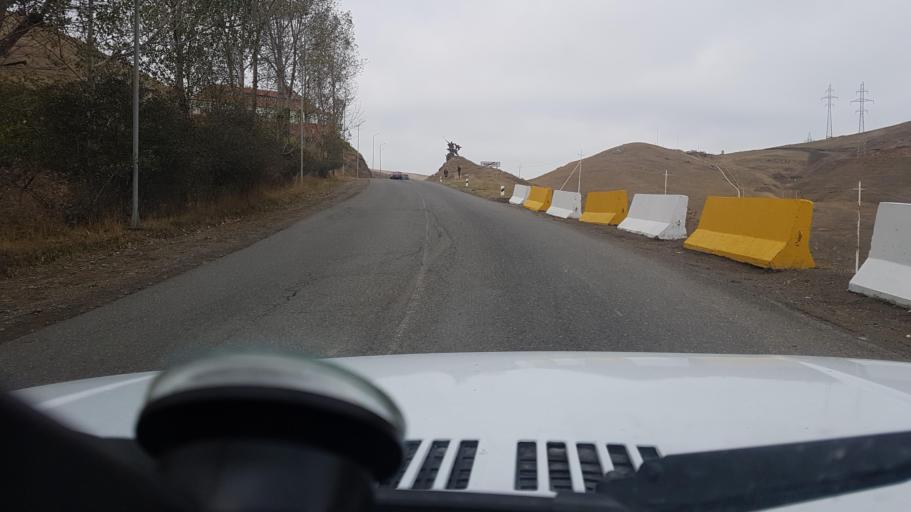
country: AZ
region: Gadabay Rayon
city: Ariqdam
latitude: 40.6124
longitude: 45.8129
